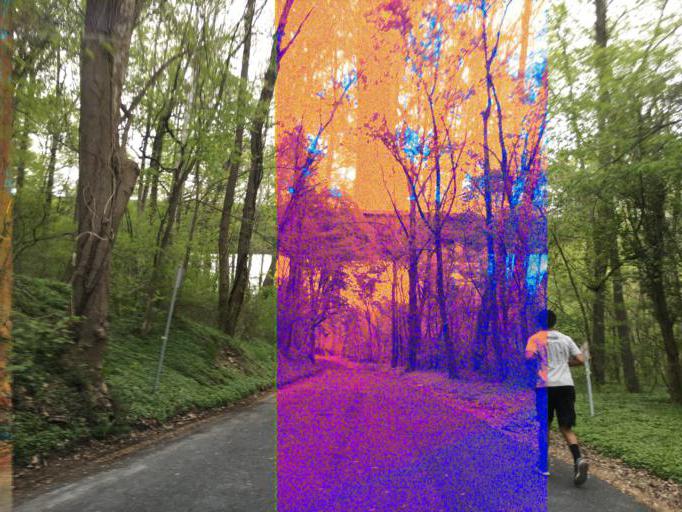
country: US
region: Maryland
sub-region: Howard County
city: Elkridge
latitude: 39.2239
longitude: -76.7167
